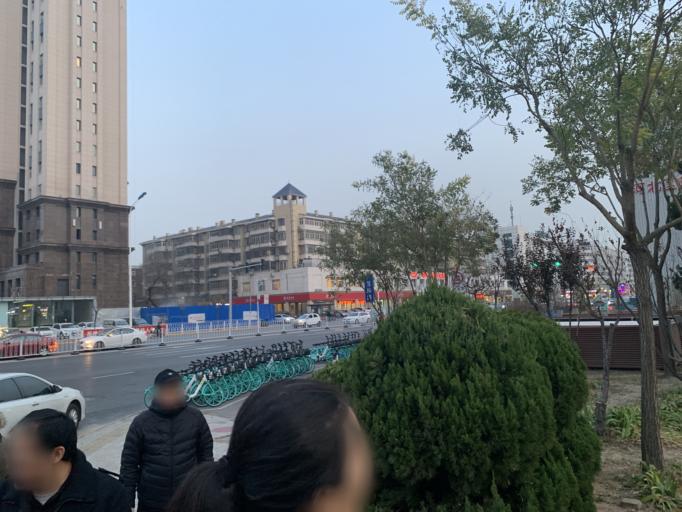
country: CN
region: Tianjin Shi
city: Wanghailou
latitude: 39.1614
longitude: 117.1986
